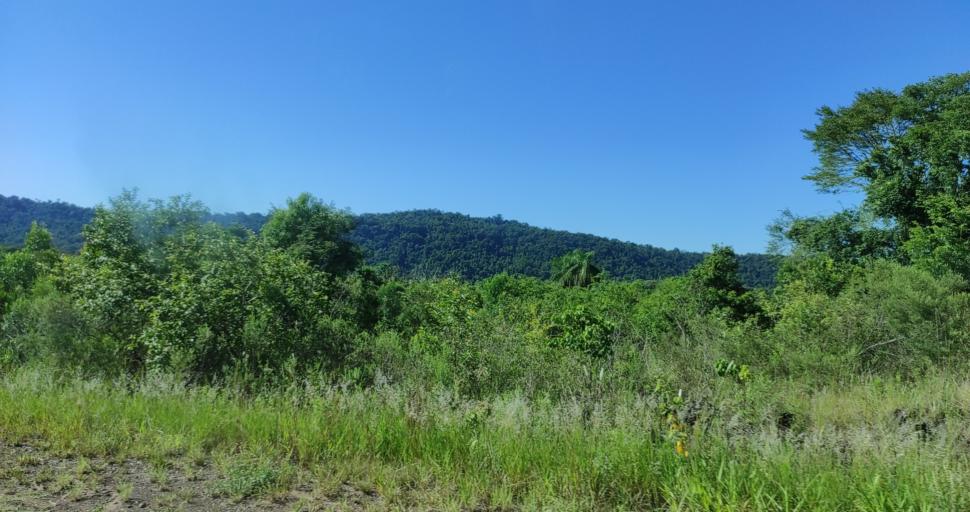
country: AR
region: Misiones
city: El Soberbio
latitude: -27.2478
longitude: -54.0351
